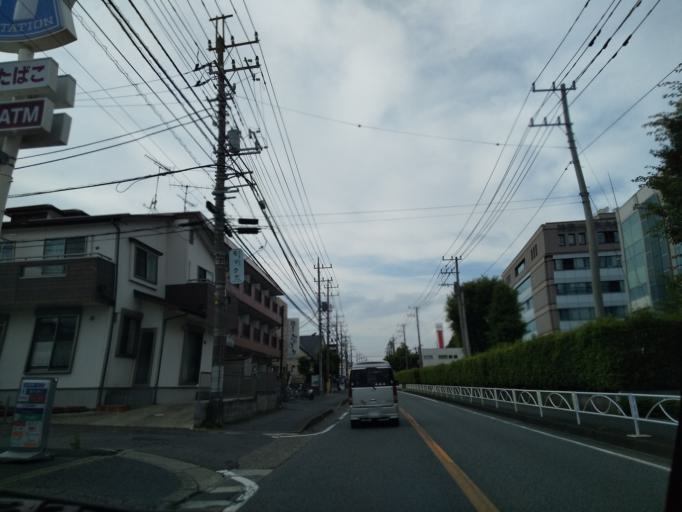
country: JP
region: Kanagawa
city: Zama
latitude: 35.4863
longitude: 139.3406
